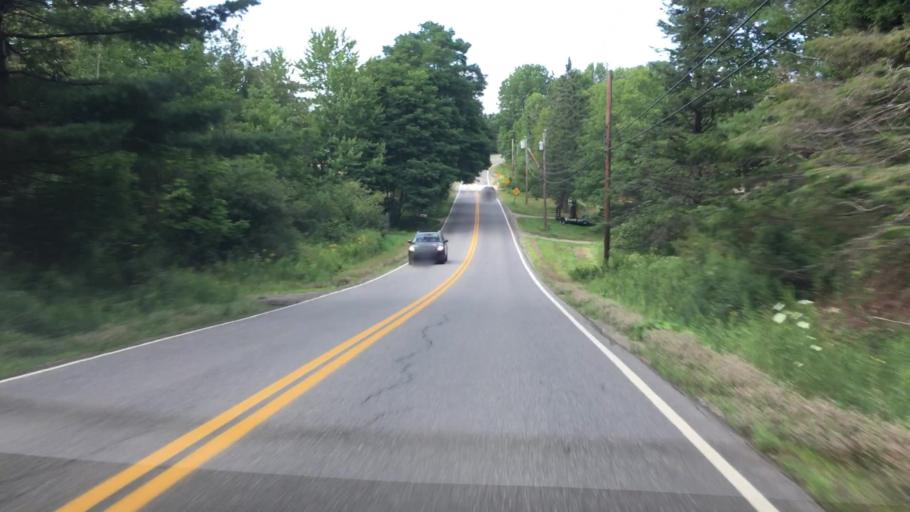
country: US
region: Maine
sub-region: Waldo County
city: Belfast
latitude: 44.4033
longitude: -69.0310
